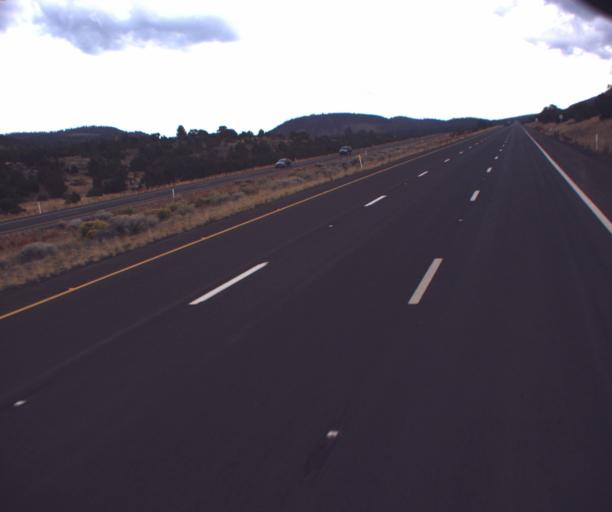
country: US
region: Arizona
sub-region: Coconino County
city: Flagstaff
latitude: 35.4218
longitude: -111.5708
